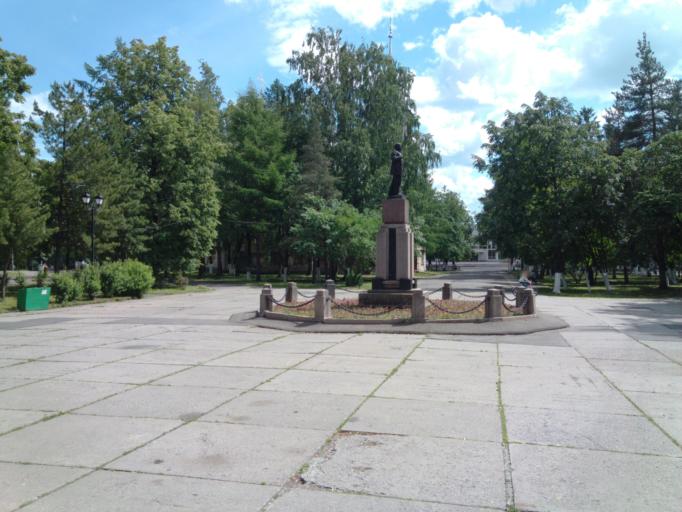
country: RU
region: Vologda
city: Vologda
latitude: 59.2184
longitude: 39.8944
